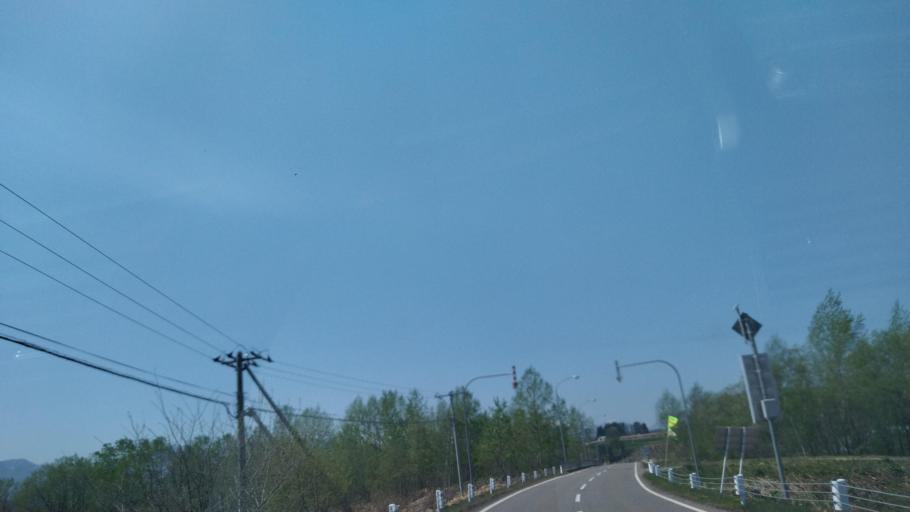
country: JP
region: Hokkaido
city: Obihiro
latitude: 42.9024
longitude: 143.0119
